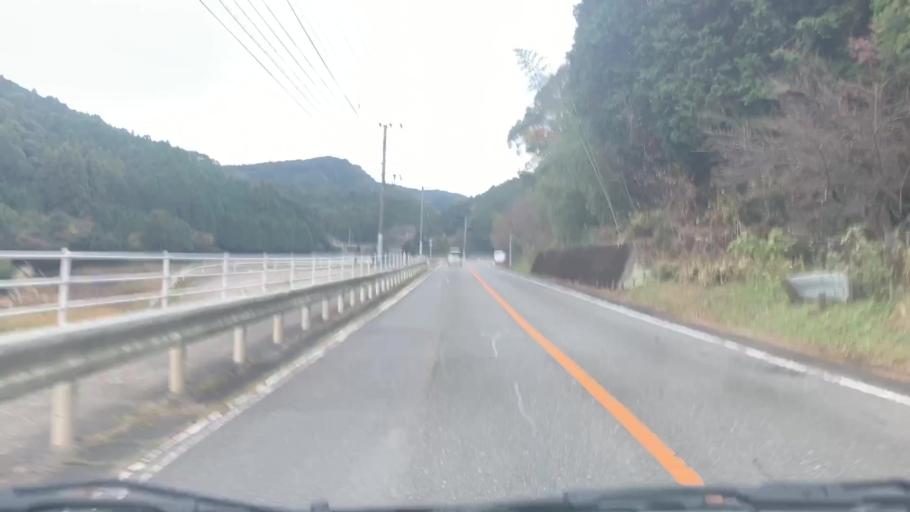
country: JP
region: Saga Prefecture
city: Ureshinomachi-shimojuku
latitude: 33.1562
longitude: 129.9719
